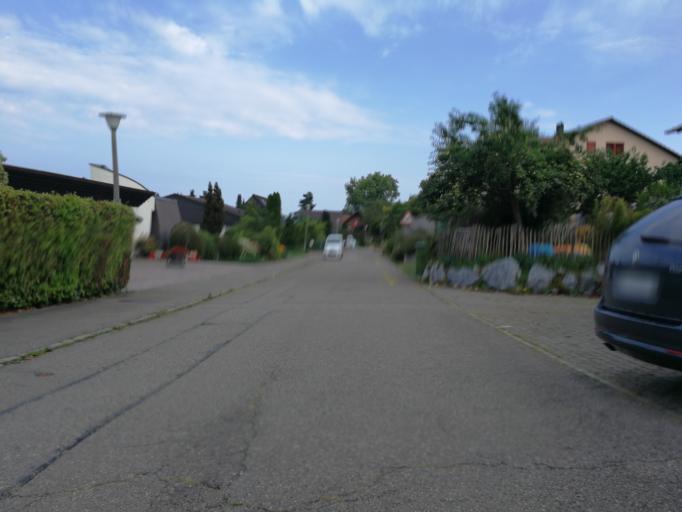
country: CH
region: Zurich
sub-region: Bezirk Hinwil
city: Wetzikon / Robenhausen
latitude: 47.3327
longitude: 8.7628
